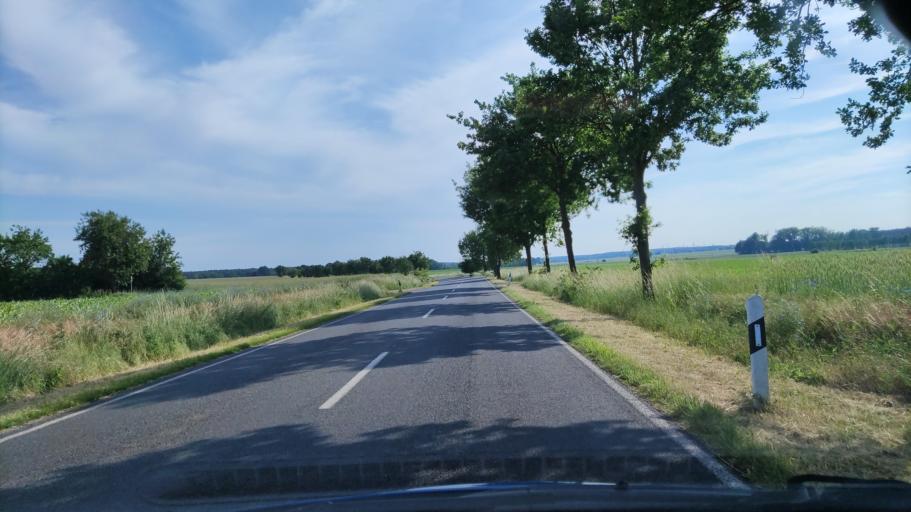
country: DE
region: Saxony-Anhalt
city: Klotze
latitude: 52.6592
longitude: 11.2005
